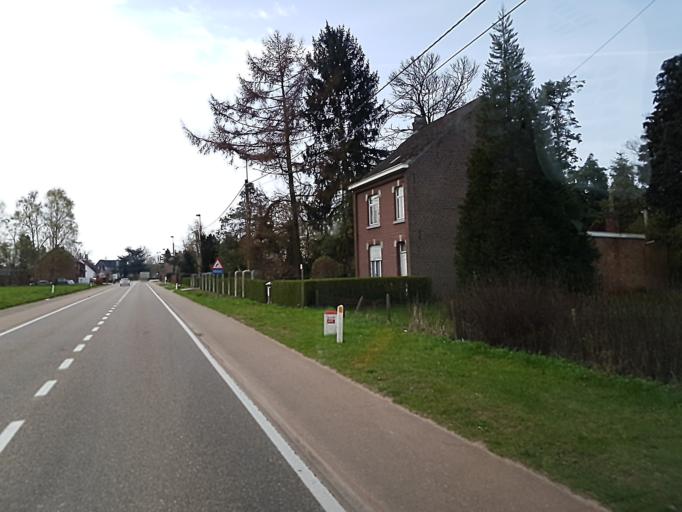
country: BE
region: Flanders
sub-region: Provincie Vlaams-Brabant
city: Scherpenheuvel-Zichem
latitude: 51.0118
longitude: 4.9909
